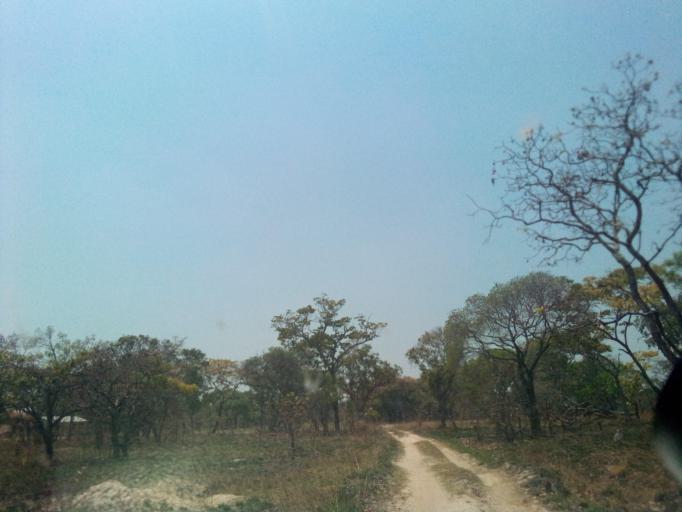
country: ZM
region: Copperbelt
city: Kataba
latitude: -12.2392
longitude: 30.4040
